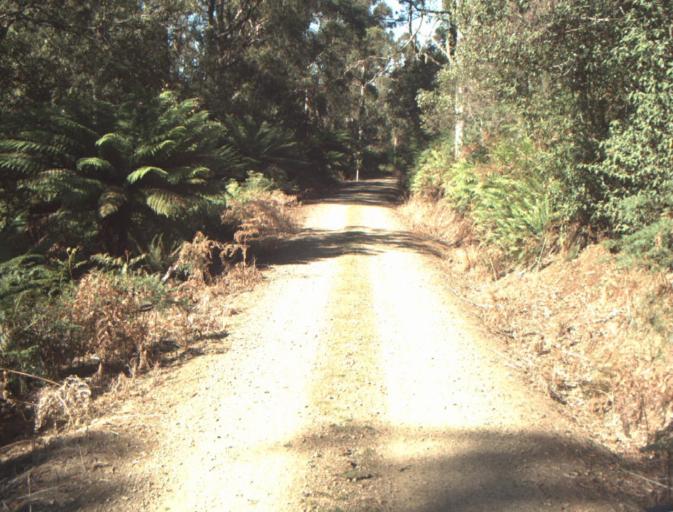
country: AU
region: Tasmania
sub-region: Dorset
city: Scottsdale
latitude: -41.2749
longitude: 147.3627
